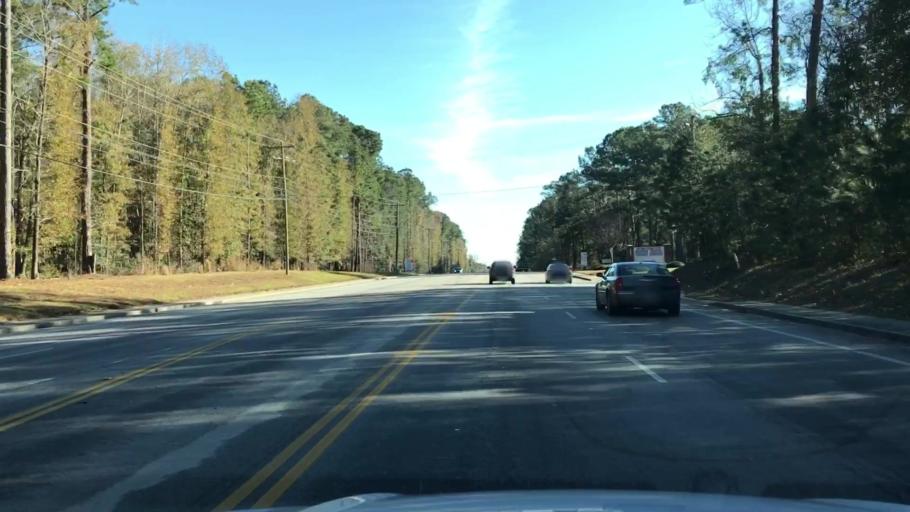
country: US
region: South Carolina
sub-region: Berkeley County
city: Ladson
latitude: 32.9842
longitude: -80.1168
